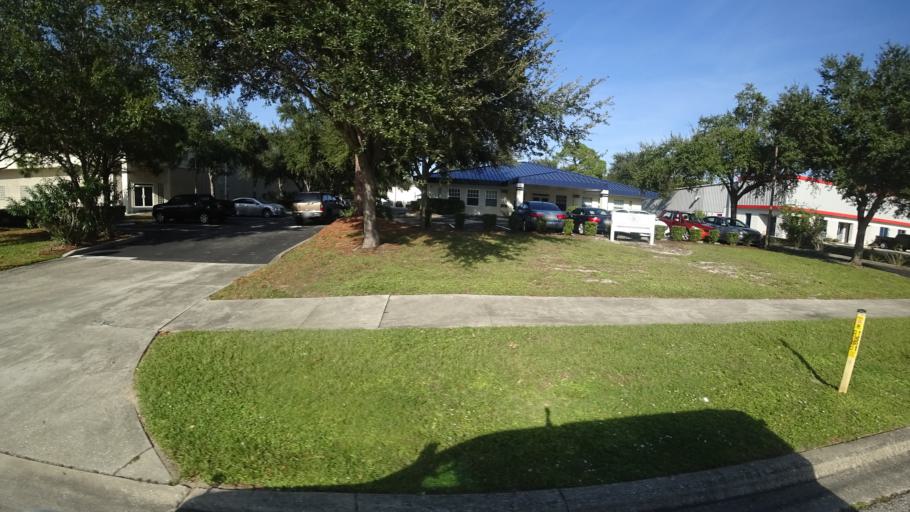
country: US
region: Florida
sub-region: Manatee County
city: Whitfield
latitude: 27.4067
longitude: -82.5564
